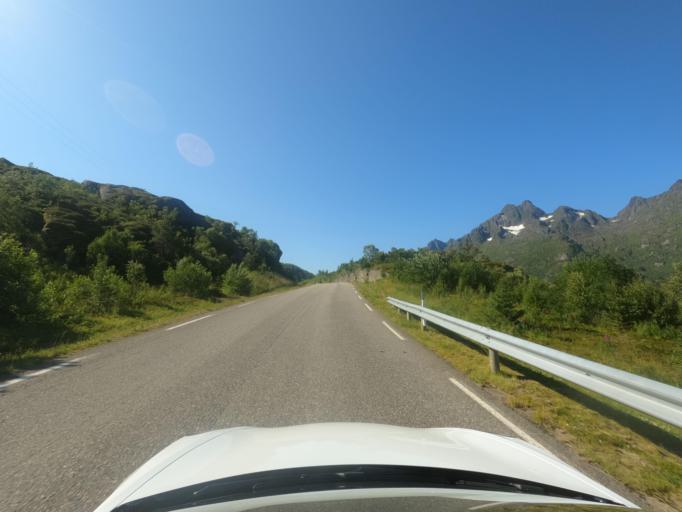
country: NO
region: Nordland
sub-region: Hadsel
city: Stokmarknes
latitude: 68.4379
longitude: 15.1847
